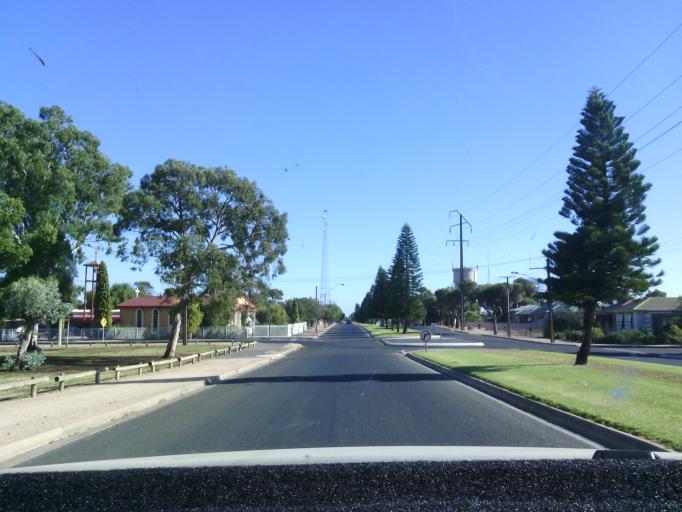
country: AU
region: South Australia
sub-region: Berri and Barmera
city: Berri
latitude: -34.2763
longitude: 140.5972
